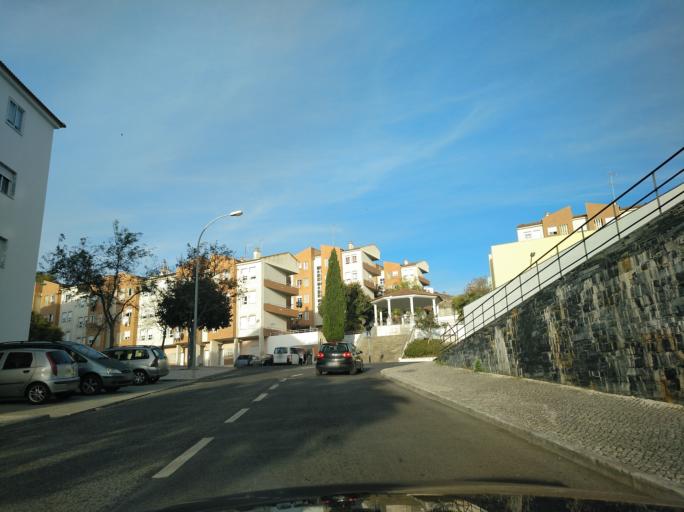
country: PT
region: Lisbon
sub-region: Oeiras
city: Linda-a-Velha
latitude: 38.7243
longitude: -9.2237
